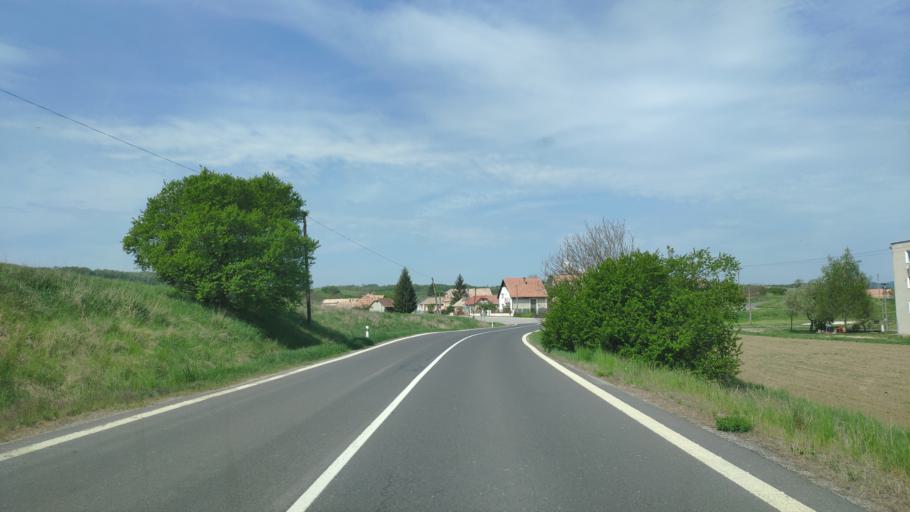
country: HU
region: Borsod-Abauj-Zemplen
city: Ozd
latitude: 48.3962
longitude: 20.2583
